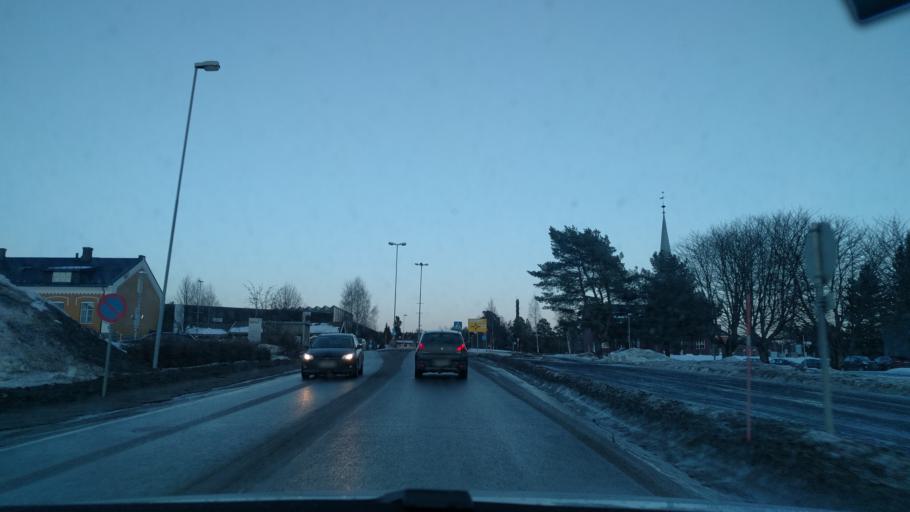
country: NO
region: Hedmark
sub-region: Elverum
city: Elverum
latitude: 60.8779
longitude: 11.5635
